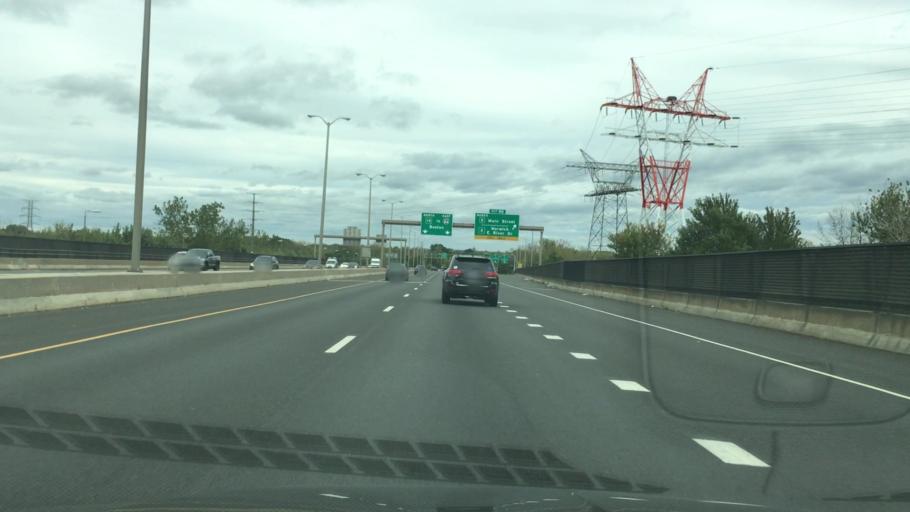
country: US
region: Connecticut
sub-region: Hartford County
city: Hartford
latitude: 41.7542
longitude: -72.6533
